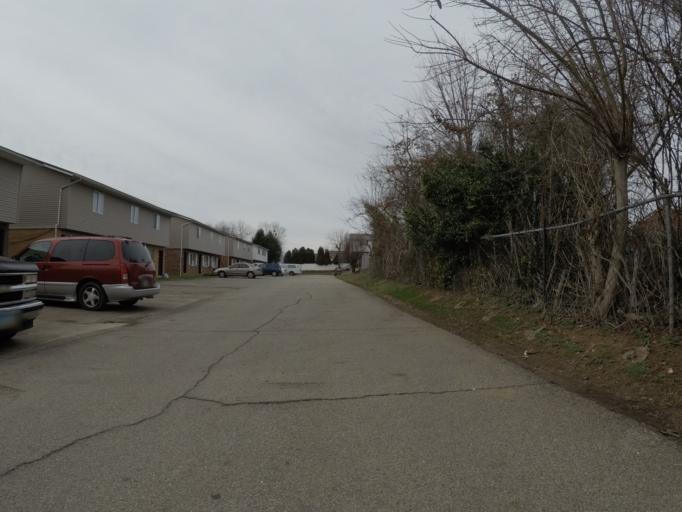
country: US
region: West Virginia
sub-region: Cabell County
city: Pea Ridge
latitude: 38.4446
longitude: -82.3408
